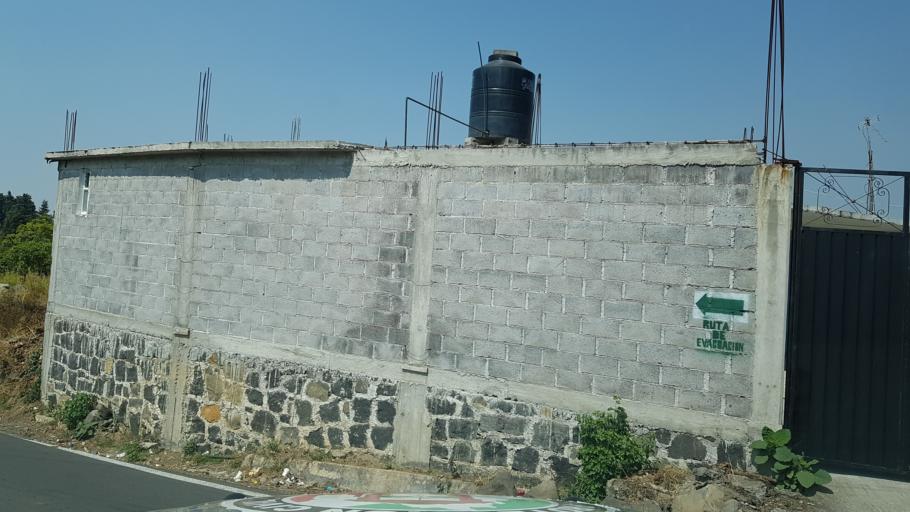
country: MX
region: Mexico
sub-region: Atlautla
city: San Juan Tepecoculco
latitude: 18.9875
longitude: -98.7908
